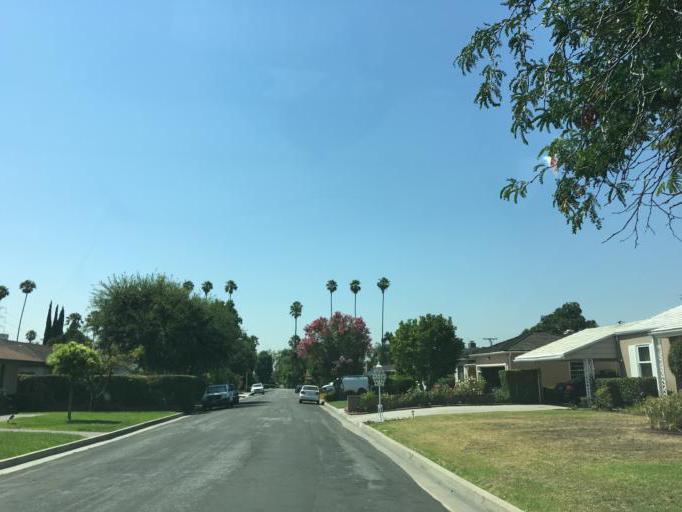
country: US
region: California
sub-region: Los Angeles County
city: San Marino
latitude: 34.1150
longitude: -118.0842
